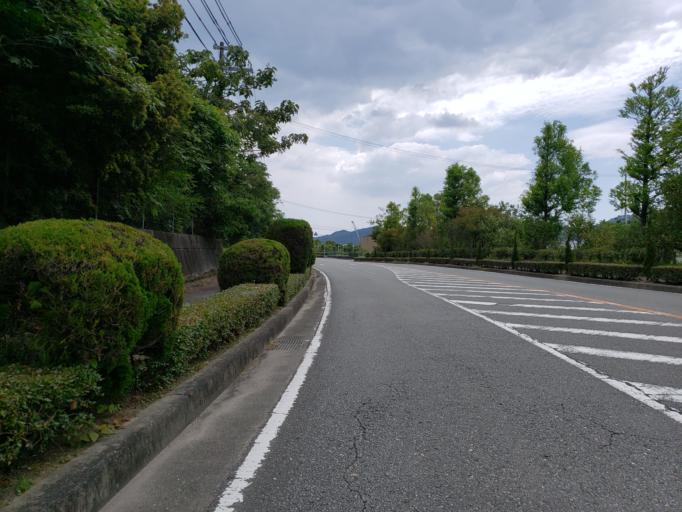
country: JP
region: Hyogo
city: Aioi
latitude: 34.7838
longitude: 134.4755
